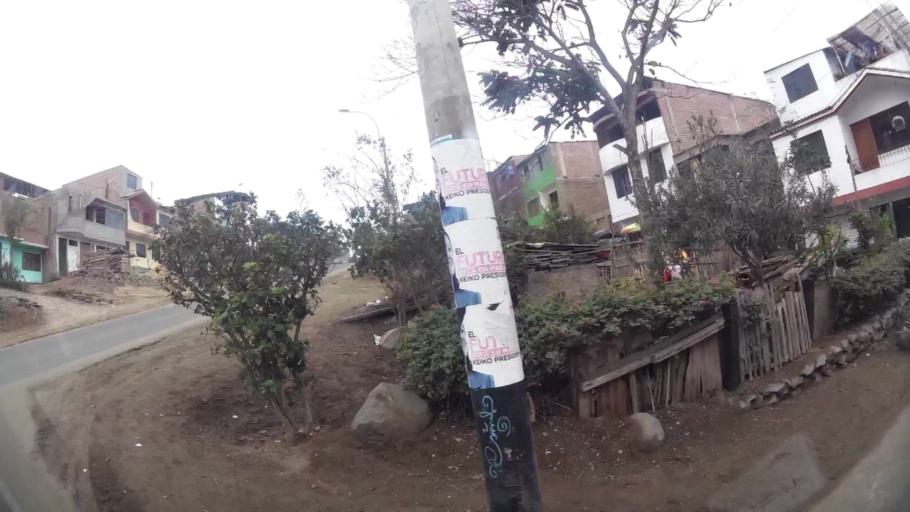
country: PE
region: Lima
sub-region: Lima
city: Surco
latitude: -12.1685
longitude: -76.9574
